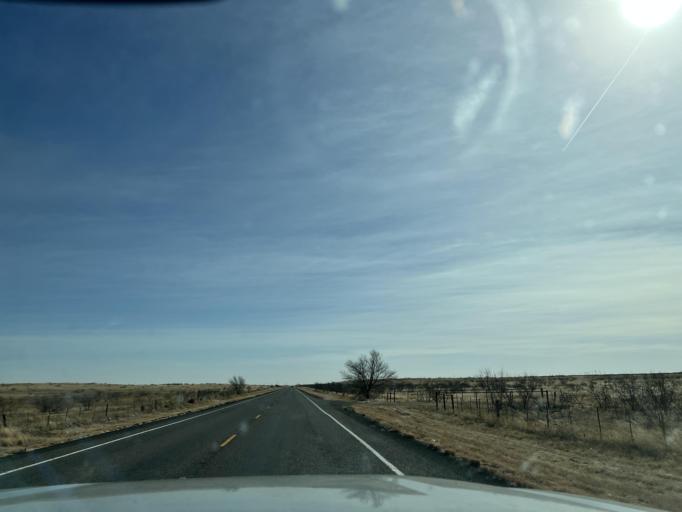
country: US
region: Texas
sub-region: Andrews County
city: Andrews
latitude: 32.4793
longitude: -102.4746
